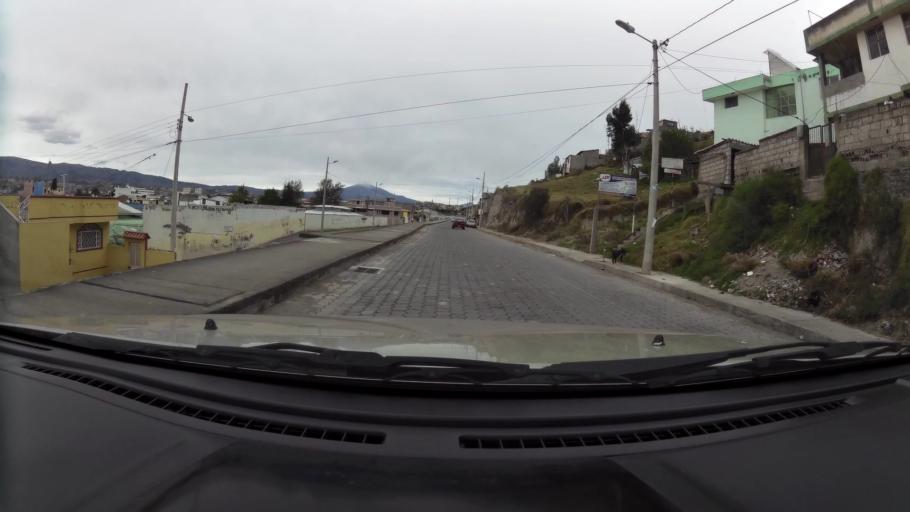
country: EC
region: Cotopaxi
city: Latacunga
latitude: -0.9367
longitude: -78.6109
